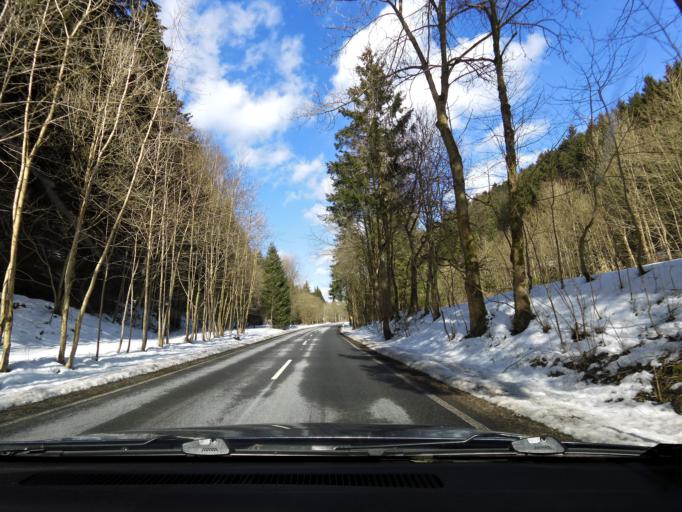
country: DE
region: Lower Saxony
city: Sankt Andreasberg
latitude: 51.6906
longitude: 10.5020
